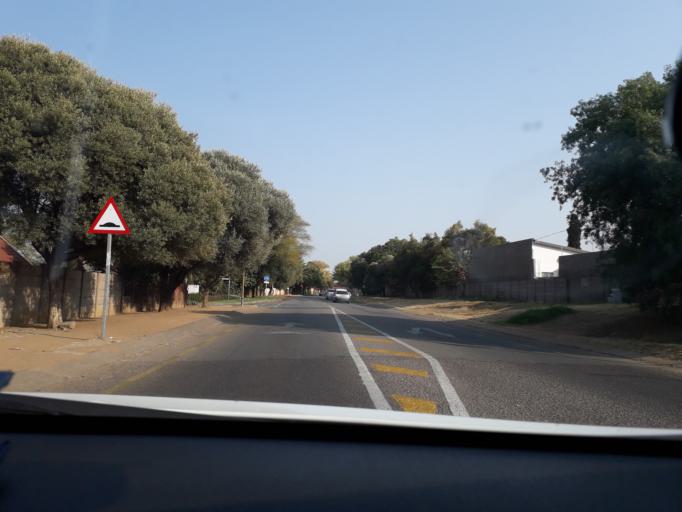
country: ZA
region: Gauteng
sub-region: City of Tshwane Metropolitan Municipality
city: Centurion
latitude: -25.8946
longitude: 28.1477
